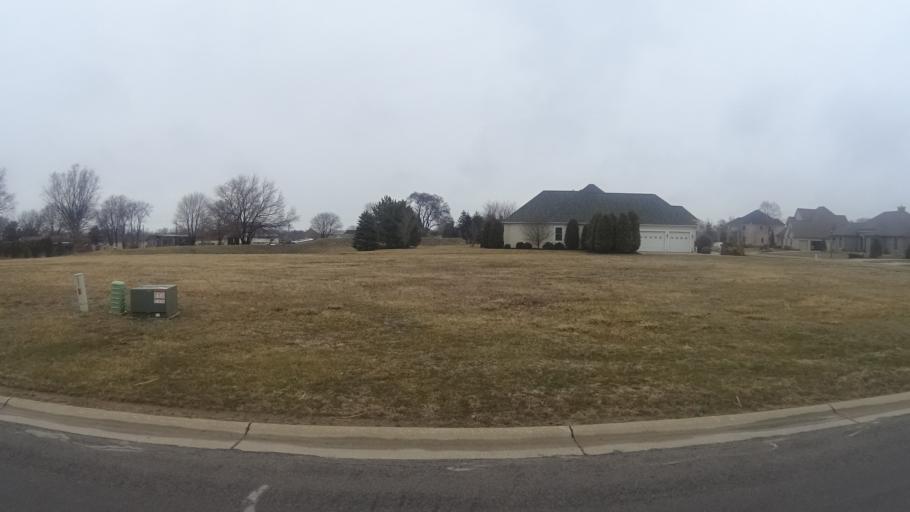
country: US
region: Ohio
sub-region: Erie County
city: Sandusky
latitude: 41.4199
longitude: -82.6525
